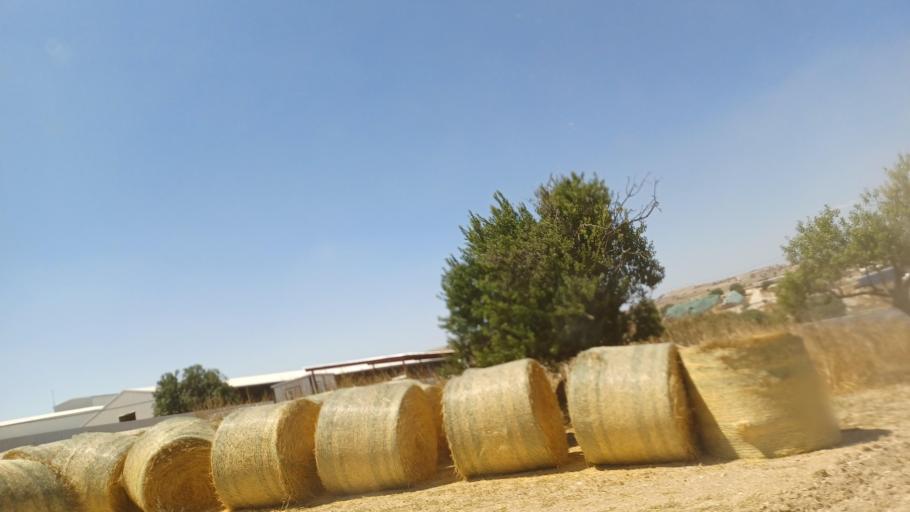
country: CY
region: Lefkosia
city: Lympia
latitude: 34.9888
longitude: 33.4746
